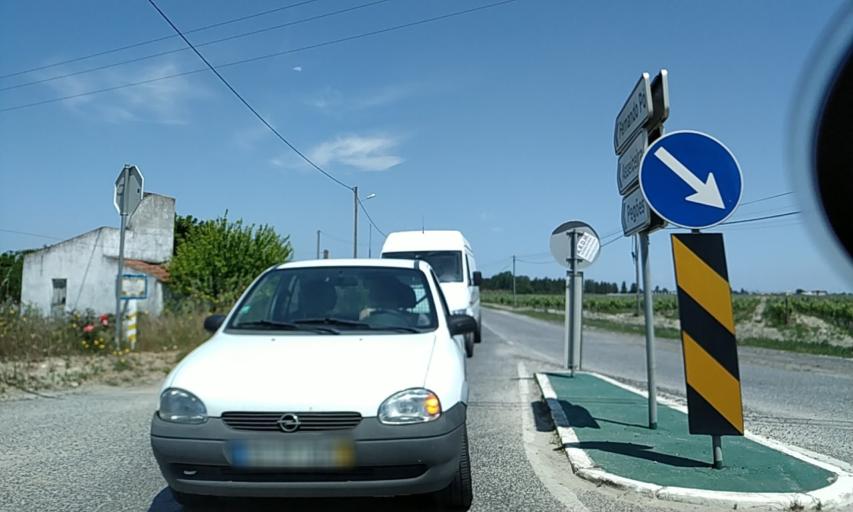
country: PT
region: Setubal
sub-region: Palmela
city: Pinhal Novo
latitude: 38.6387
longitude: -8.7422
